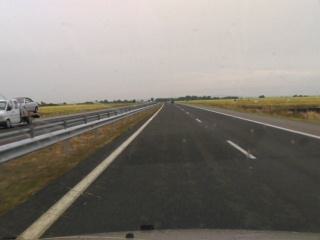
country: BG
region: Stara Zagora
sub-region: Obshtina Radnevo
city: Radnevo
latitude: 42.3869
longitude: 25.8714
